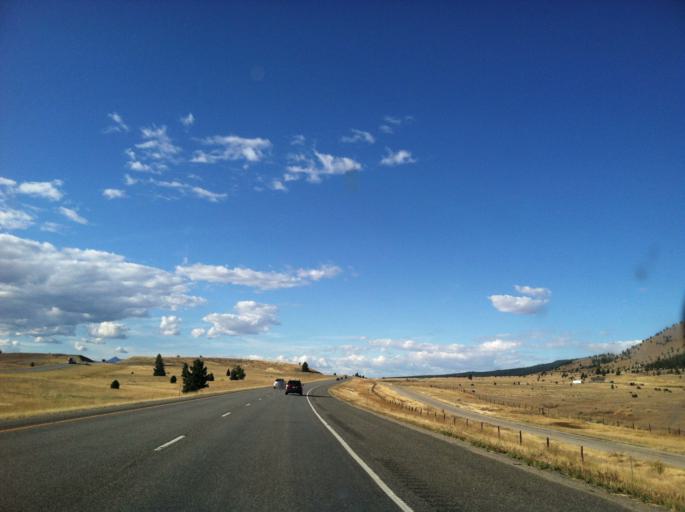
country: US
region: Montana
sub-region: Silver Bow County
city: Butte-Silver Bow (Balance)
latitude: 46.0319
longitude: -112.7320
